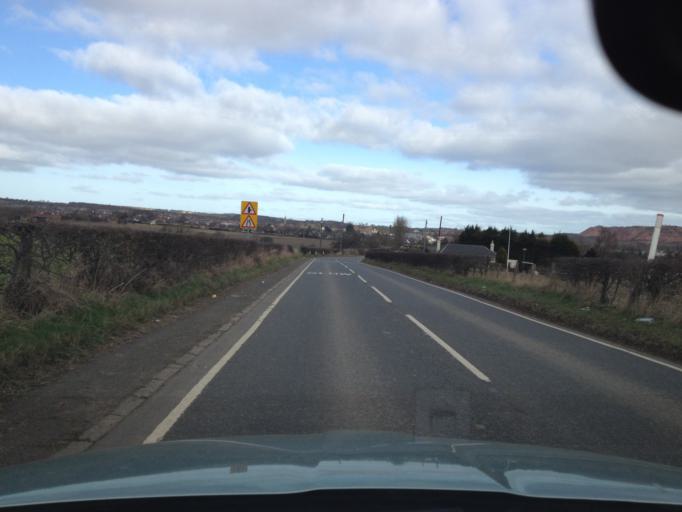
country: GB
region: Scotland
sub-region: West Lothian
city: Broxburn
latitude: 55.9243
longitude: -3.4673
